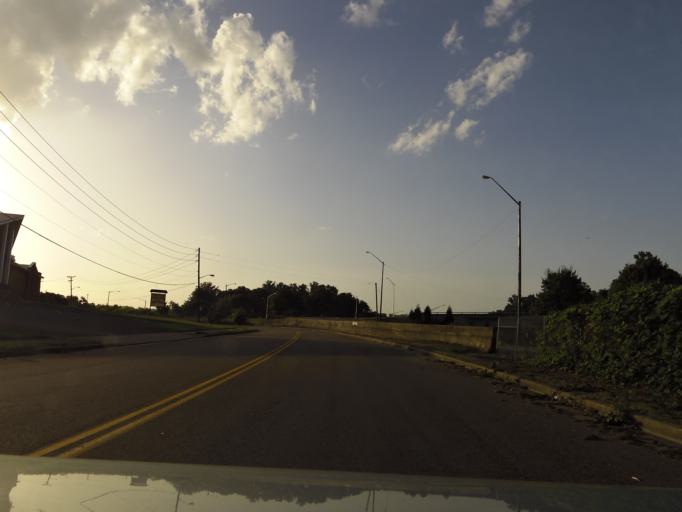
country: US
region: Tennessee
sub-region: Knox County
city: Knoxville
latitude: 35.9567
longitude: -83.8973
